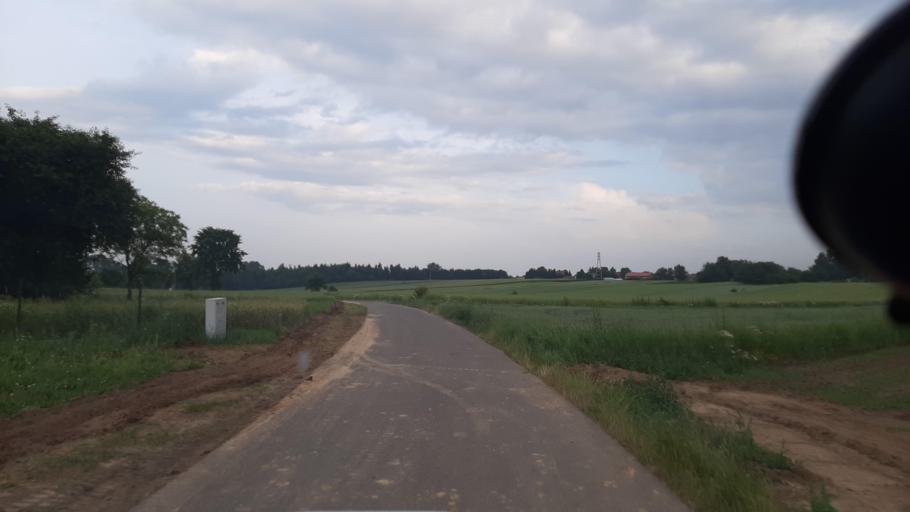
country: PL
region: Lublin Voivodeship
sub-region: Powiat lubelski
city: Garbow
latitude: 51.3518
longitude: 22.3583
